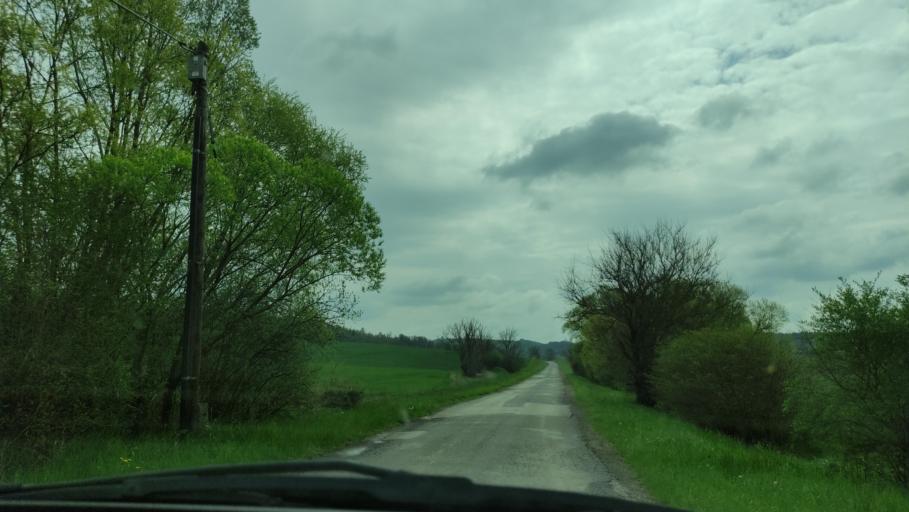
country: HU
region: Baranya
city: Magocs
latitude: 46.3060
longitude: 18.1890
